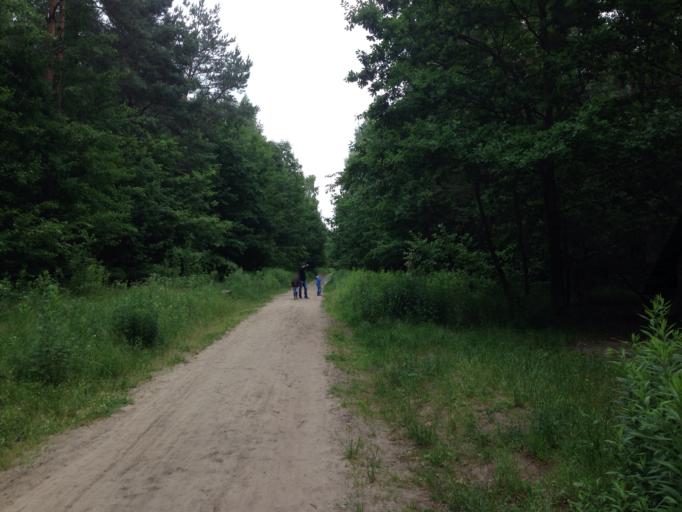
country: PL
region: Masovian Voivodeship
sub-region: Powiat warszawski zachodni
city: Babice
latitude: 52.2555
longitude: 20.8692
